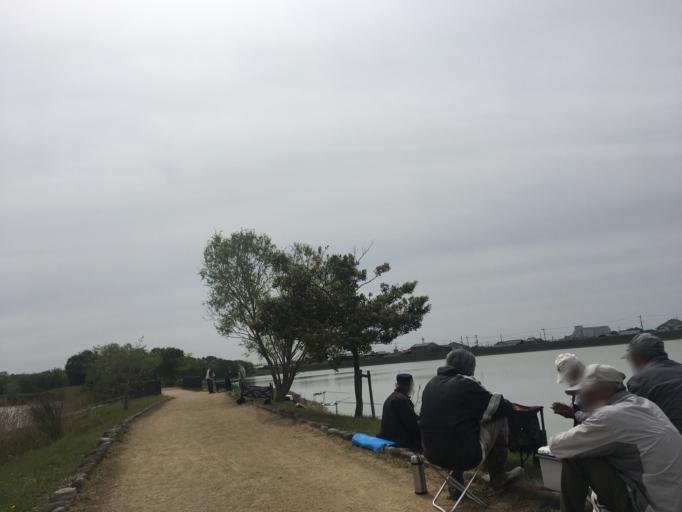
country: JP
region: Hyogo
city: Miki
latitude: 34.7640
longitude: 134.9236
